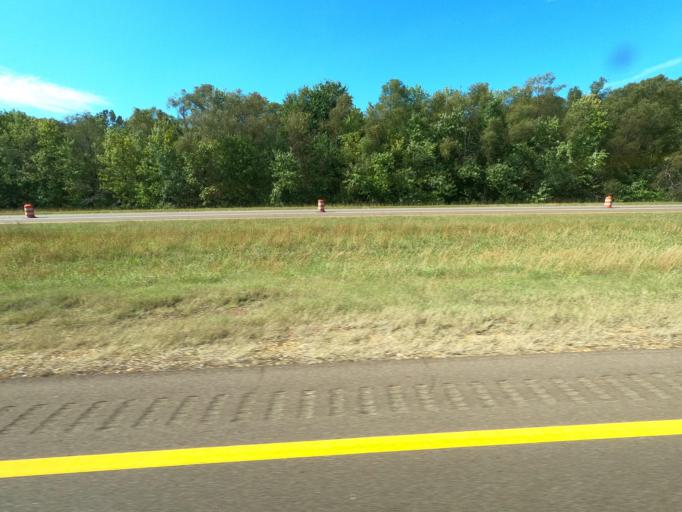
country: US
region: Tennessee
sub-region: Dyer County
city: Dyersburg
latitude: 35.9910
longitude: -89.3424
